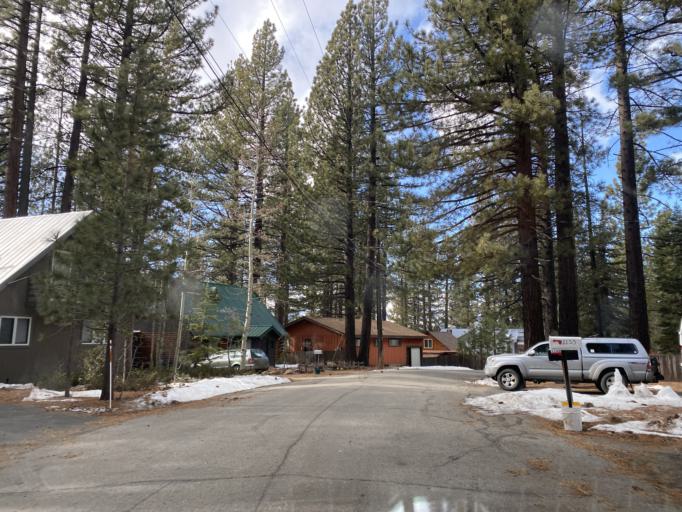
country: US
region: California
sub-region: El Dorado County
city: South Lake Tahoe
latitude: 38.9194
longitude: -119.9852
